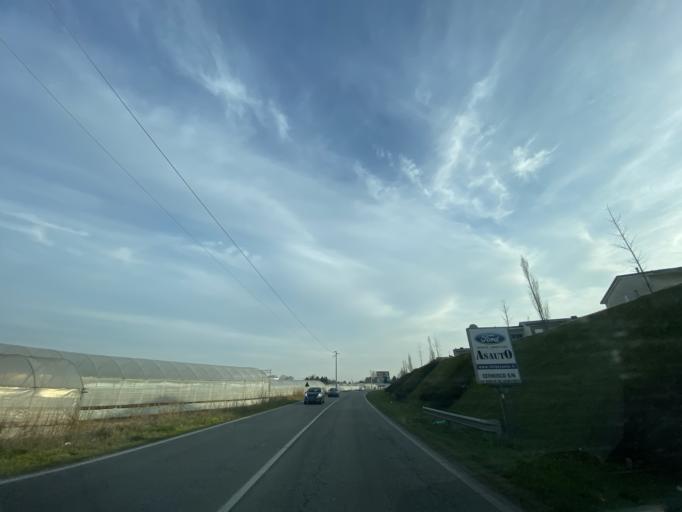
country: IT
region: Lombardy
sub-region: Citta metropolitana di Milano
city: Ronco
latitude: 45.5307
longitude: 9.3482
